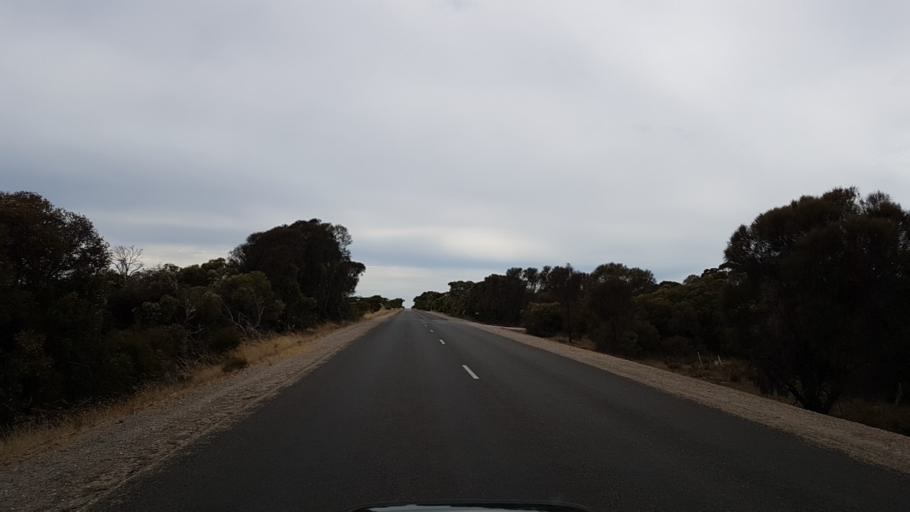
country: AU
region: South Australia
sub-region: Yorke Peninsula
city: Honiton
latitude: -34.9876
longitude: 137.1422
